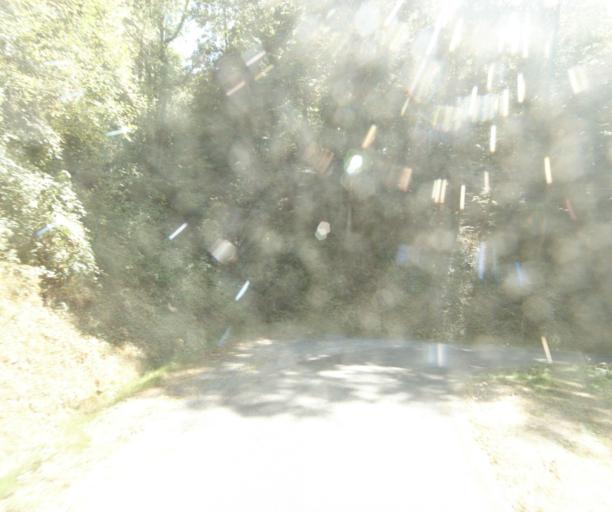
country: FR
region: Rhone-Alpes
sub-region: Departement du Rhone
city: Sainte-Foy-l'Argentiere
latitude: 45.7236
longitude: 4.5221
